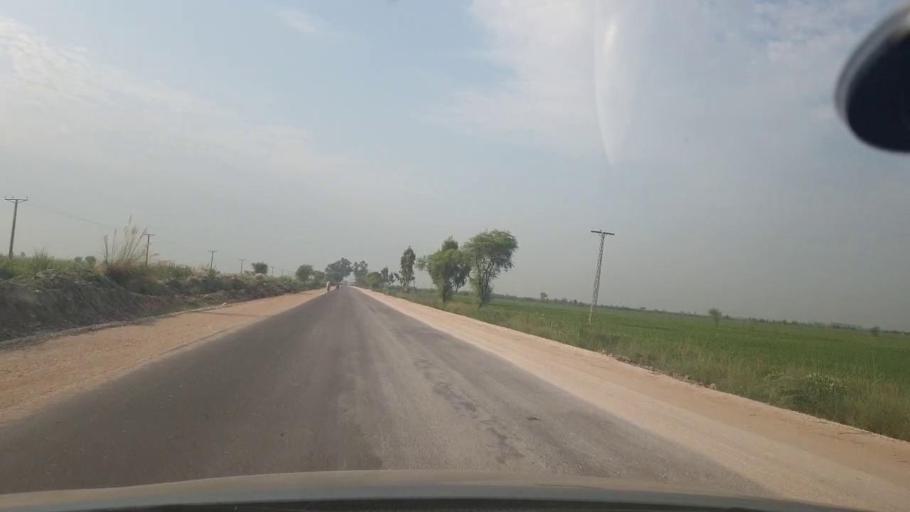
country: PK
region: Sindh
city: Jacobabad
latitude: 28.1884
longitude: 68.3675
